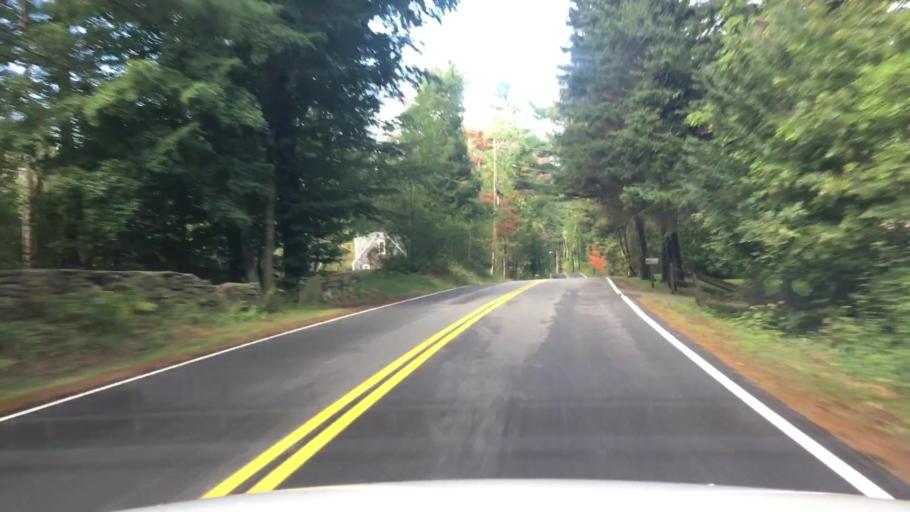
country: US
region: Maine
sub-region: York County
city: Kittery Point
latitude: 43.0895
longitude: -70.7054
